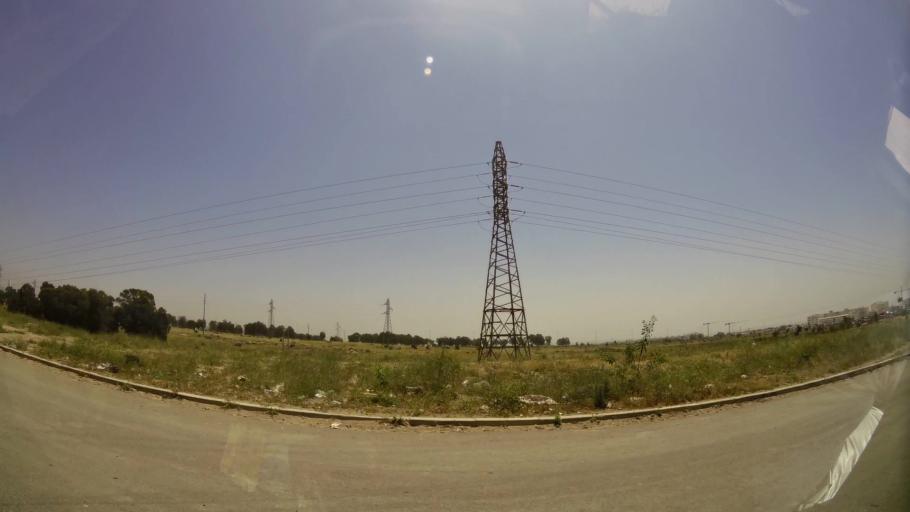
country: MA
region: Oued ed Dahab-Lagouira
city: Dakhla
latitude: 30.4252
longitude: -9.5528
